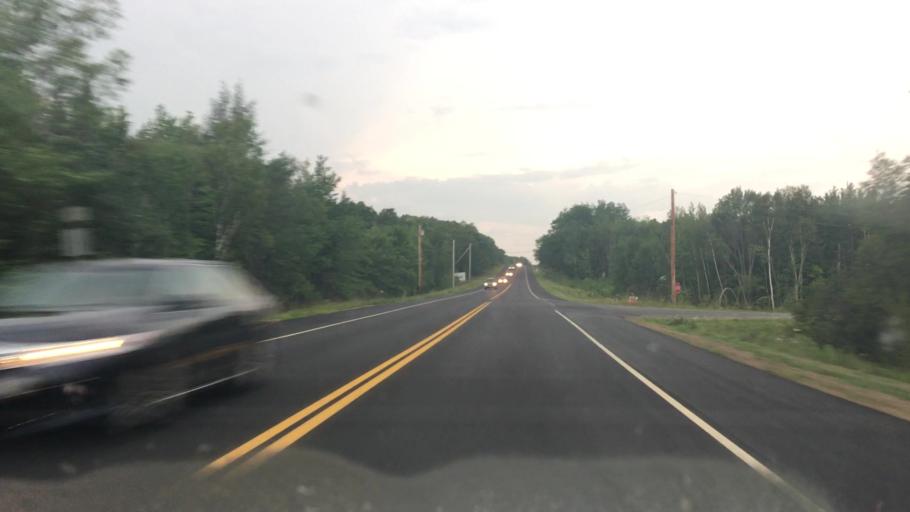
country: US
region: Maine
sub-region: Waldo County
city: Palermo
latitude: 44.3808
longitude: -69.4057
